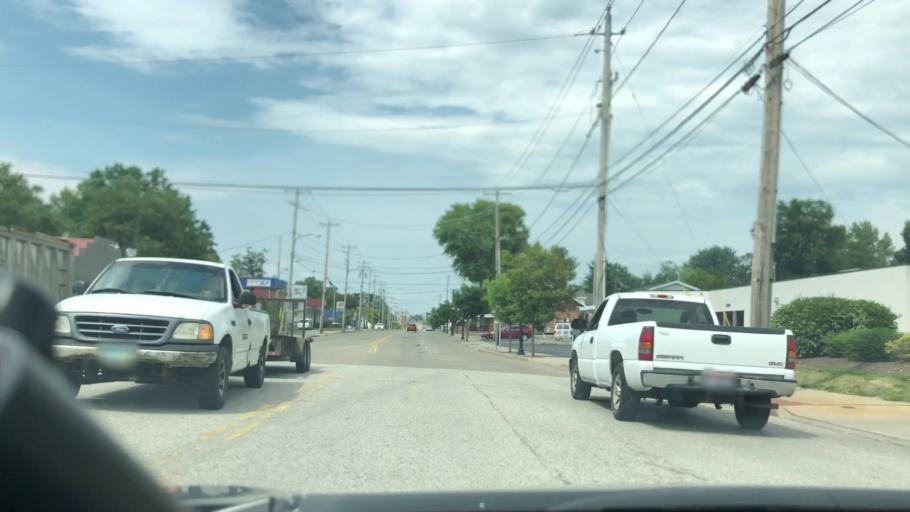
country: US
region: Ohio
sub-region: Summit County
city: Portage Lakes
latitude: 41.0293
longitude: -81.5269
